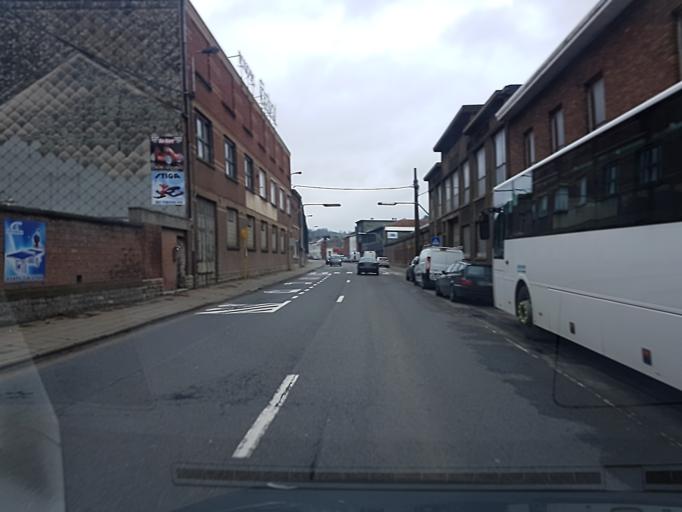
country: BE
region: Wallonia
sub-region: Province de Liege
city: Pepinster
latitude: 50.5696
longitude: 5.8167
